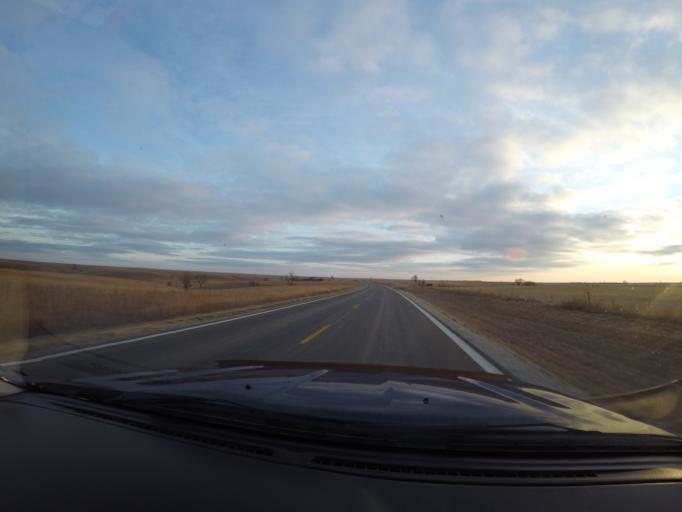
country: US
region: Kansas
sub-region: Morris County
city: Council Grove
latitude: 38.5627
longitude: -96.5222
